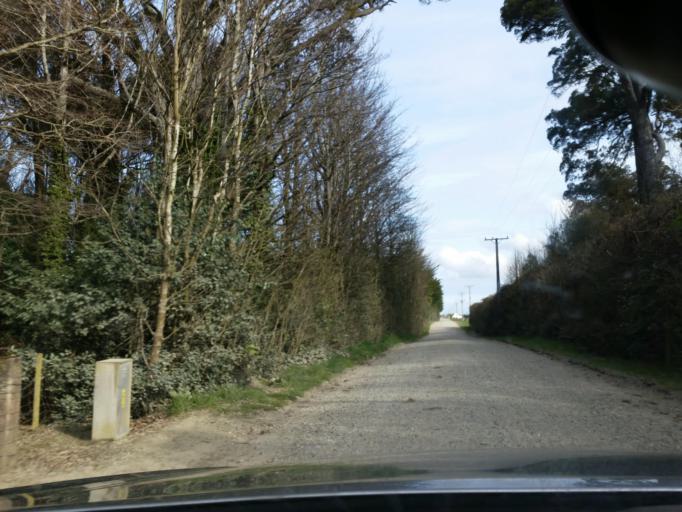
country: NZ
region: Southland
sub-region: Invercargill City
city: Invercargill
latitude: -46.3220
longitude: 168.4788
